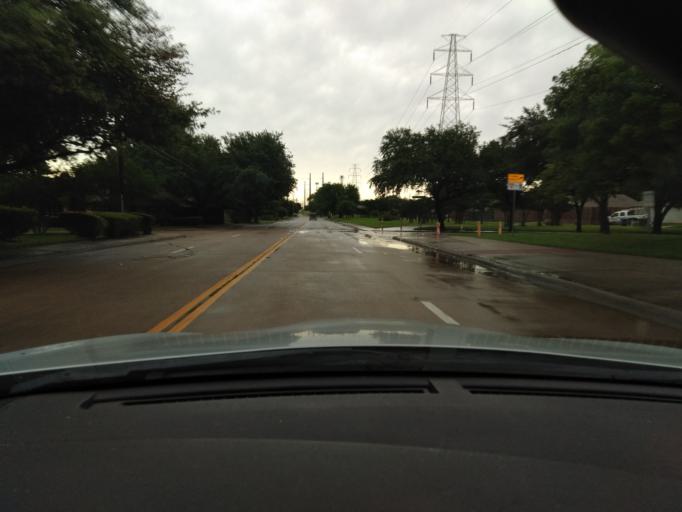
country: US
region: Texas
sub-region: Dallas County
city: Addison
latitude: 32.9726
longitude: -96.7785
